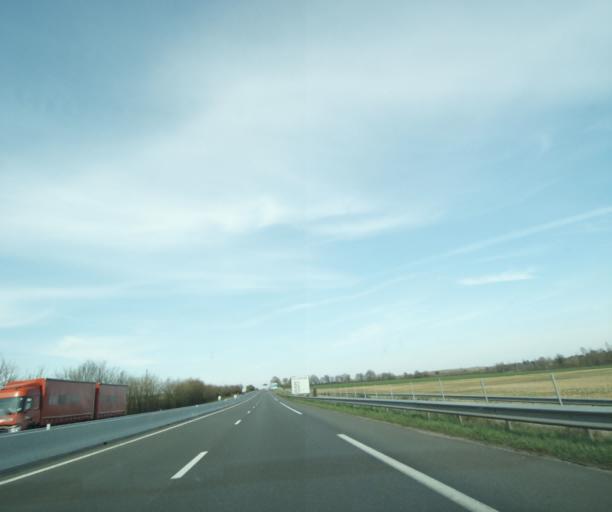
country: FR
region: Centre
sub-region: Departement du Cher
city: Massay
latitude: 47.1805
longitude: 2.0122
